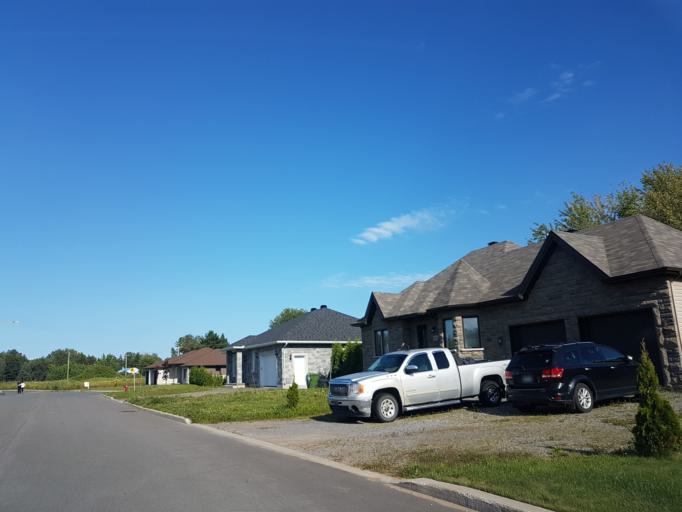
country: CA
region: Quebec
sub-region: Mauricie
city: Nicolet
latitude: 46.2887
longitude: -72.6431
